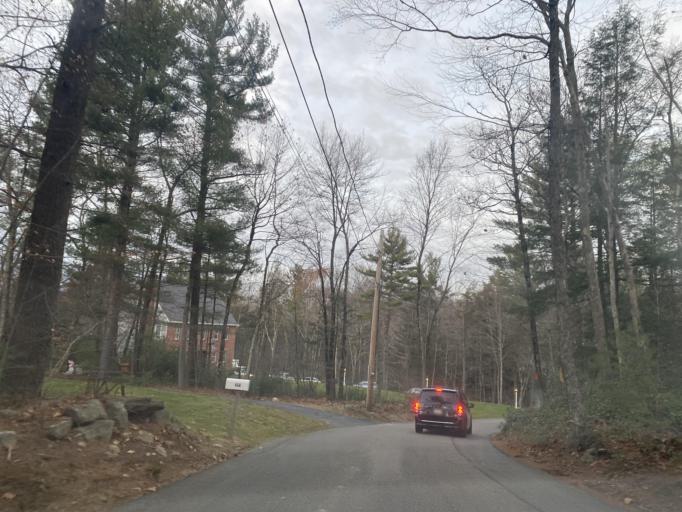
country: US
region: Massachusetts
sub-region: Worcester County
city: Paxton
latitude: 42.2749
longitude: -71.9339
